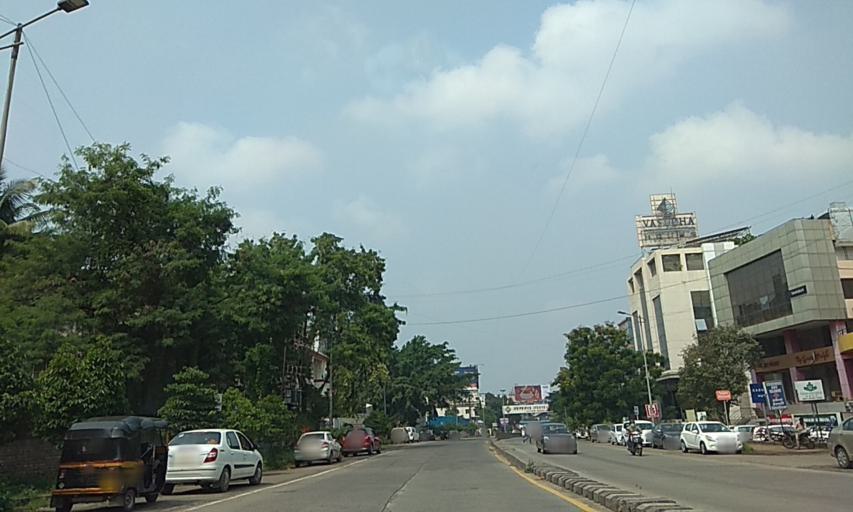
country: IN
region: Maharashtra
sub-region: Pune Division
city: Khadki
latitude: 18.5593
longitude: 73.7906
